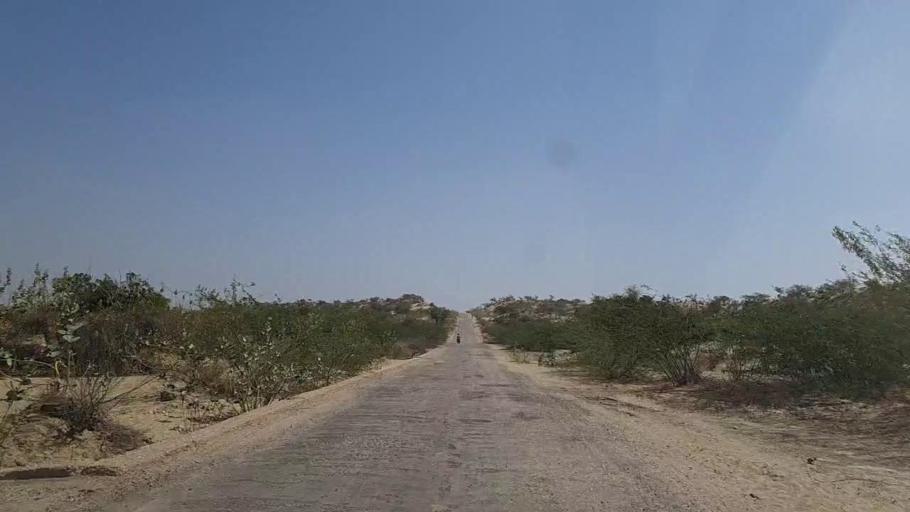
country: PK
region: Sindh
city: Diplo
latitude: 24.5136
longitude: 69.4056
